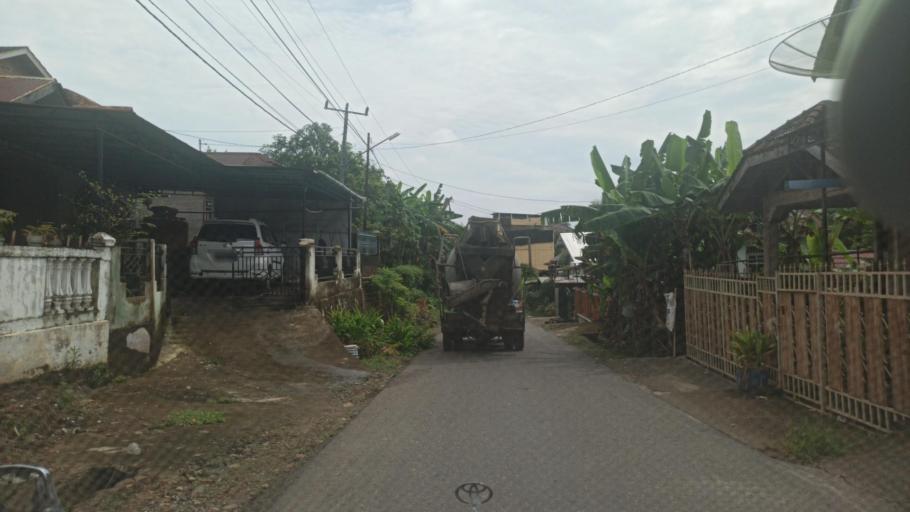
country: ID
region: South Sumatra
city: Gunungmegang Dalam
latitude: -3.2666
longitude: 103.8143
